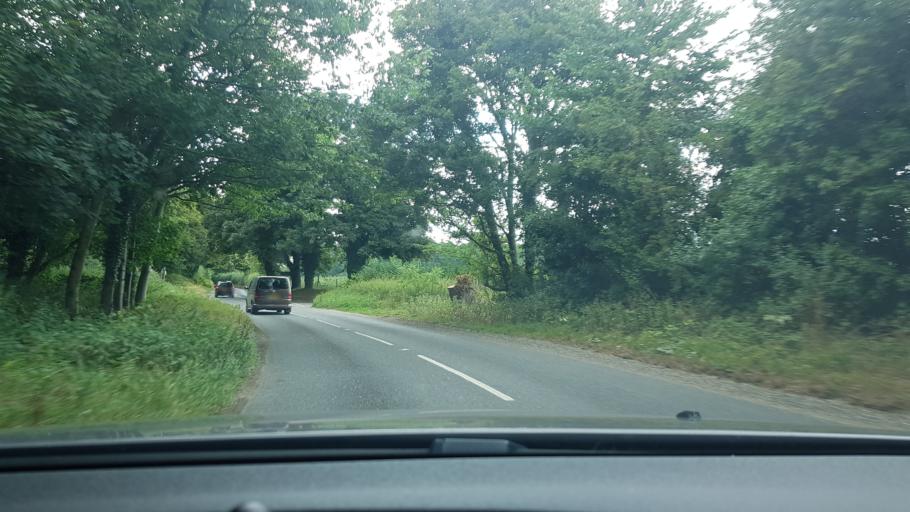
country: GB
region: England
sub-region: West Berkshire
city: Basildon
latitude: 51.4695
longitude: -1.1730
